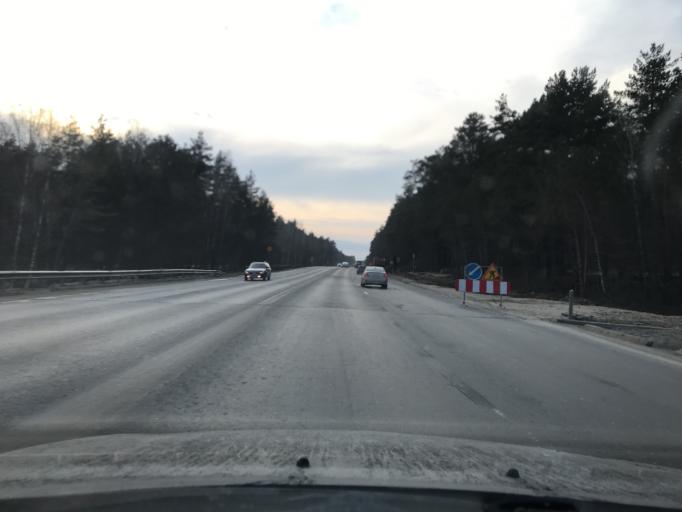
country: RU
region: Kaluga
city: Mstikhino
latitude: 54.5771
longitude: 36.0998
